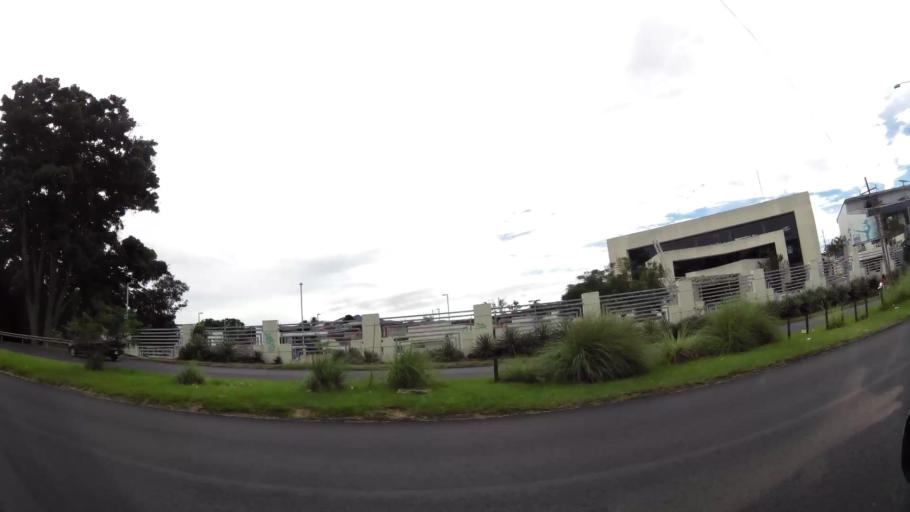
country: CR
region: San Jose
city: San Pedro
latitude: 9.9262
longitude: -84.0557
